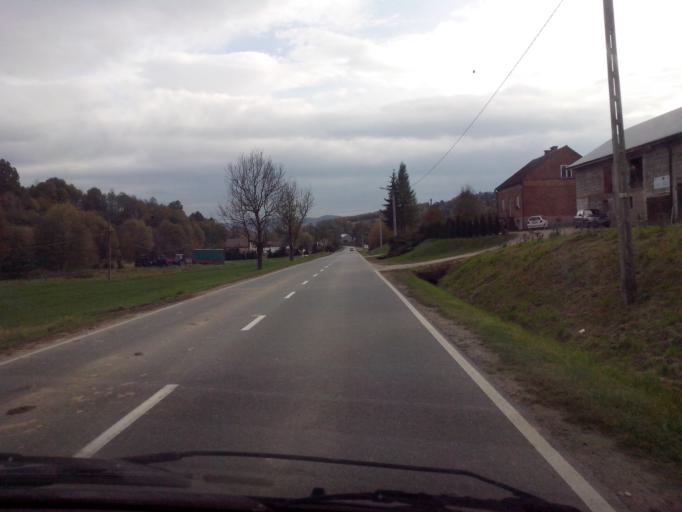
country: PL
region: Subcarpathian Voivodeship
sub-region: Powiat strzyzowski
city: Wisniowa
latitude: 49.8938
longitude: 21.6433
